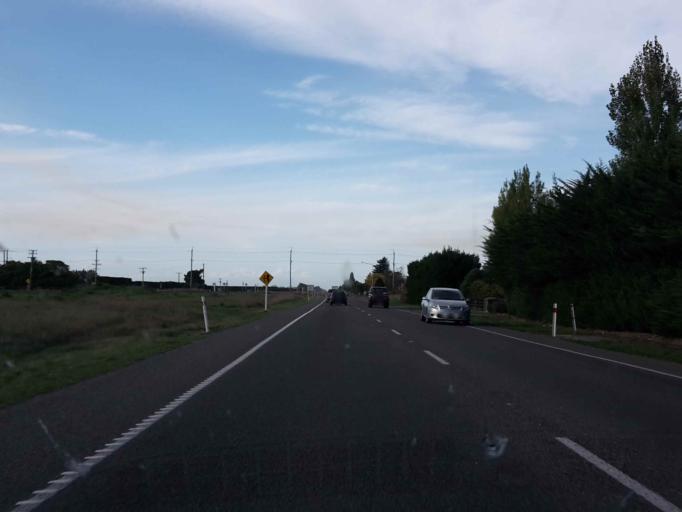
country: NZ
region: Canterbury
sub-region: Ashburton District
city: Tinwald
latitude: -43.9549
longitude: 171.6560
